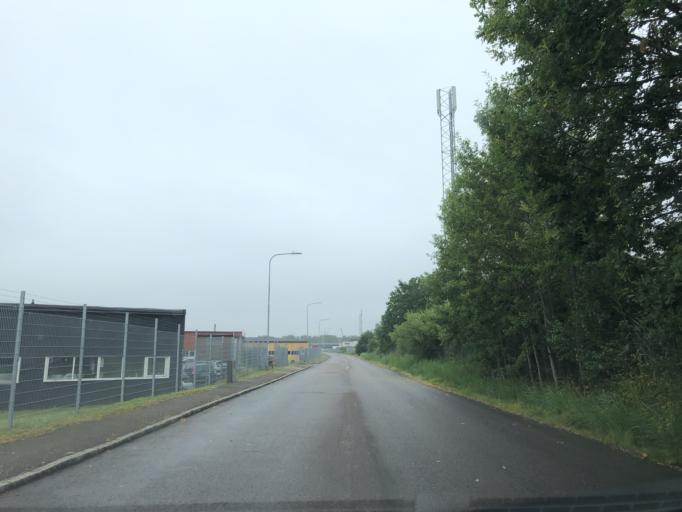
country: SE
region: Vaestra Goetaland
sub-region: Goteborg
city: Goeteborg
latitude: 57.7368
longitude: 11.9478
